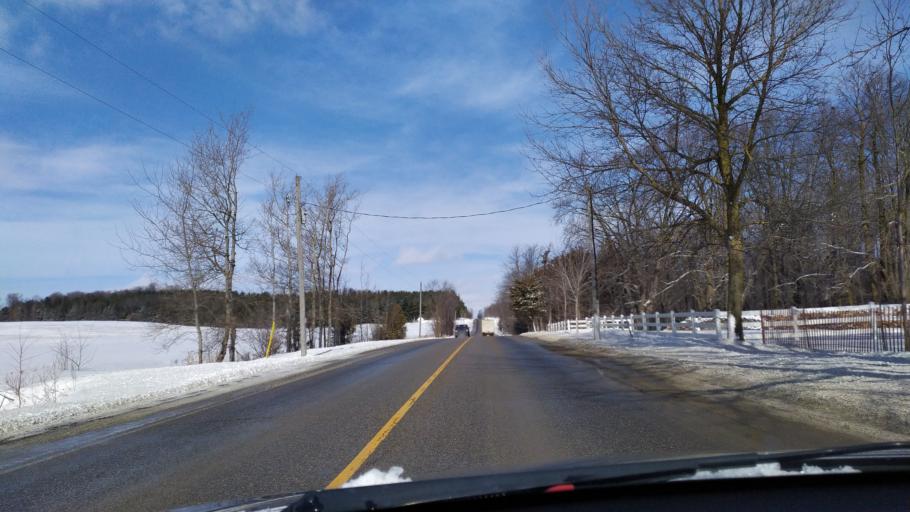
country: CA
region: Ontario
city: Waterloo
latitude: 43.5099
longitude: -80.6846
